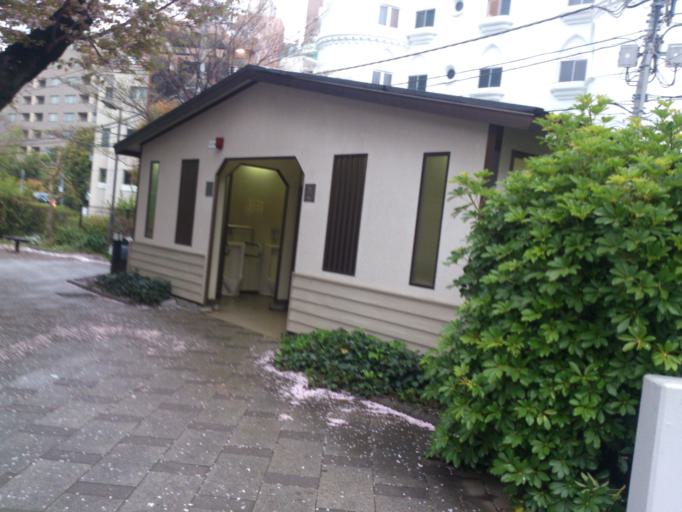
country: JP
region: Tokyo
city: Tokyo
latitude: 35.6707
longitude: 139.7371
